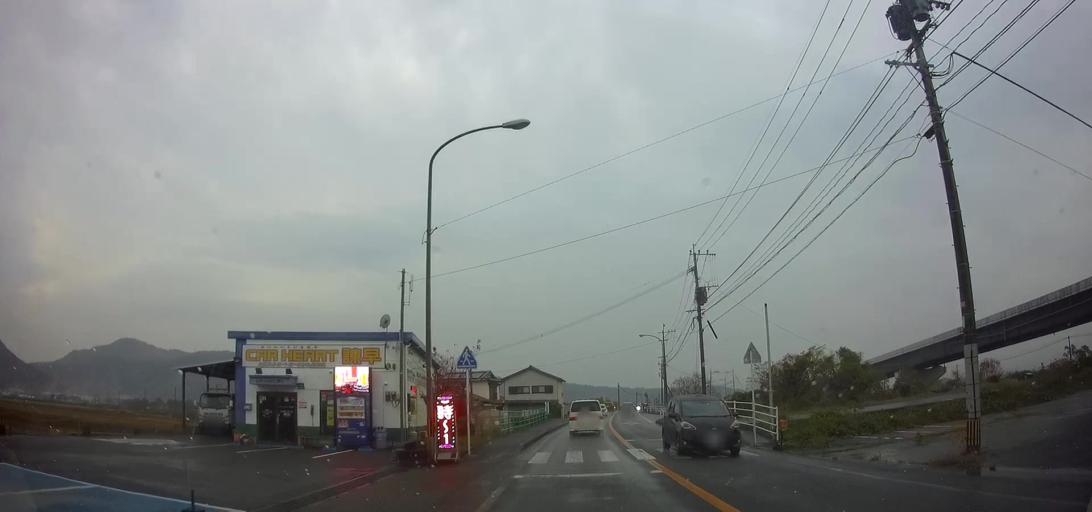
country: JP
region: Nagasaki
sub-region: Isahaya-shi
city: Isahaya
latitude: 32.8342
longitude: 130.1240
